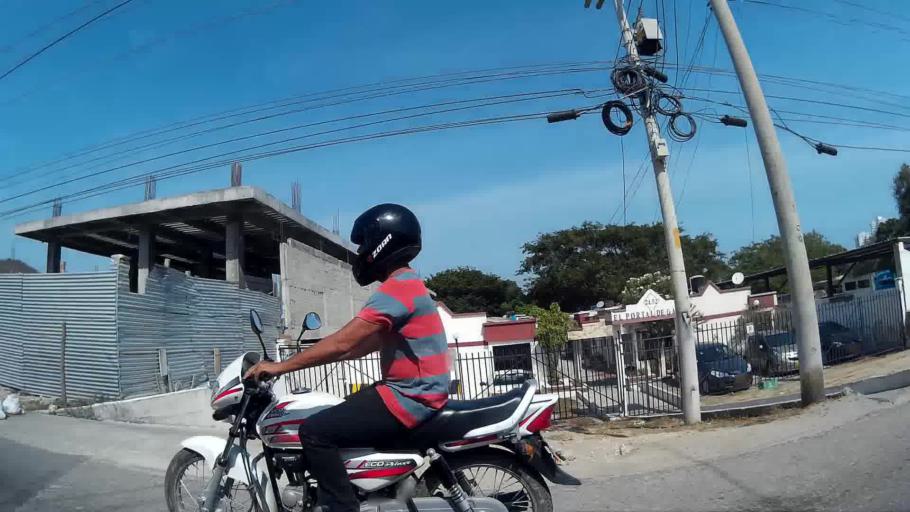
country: CO
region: Magdalena
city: Santa Marta
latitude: 11.1891
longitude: -74.2255
